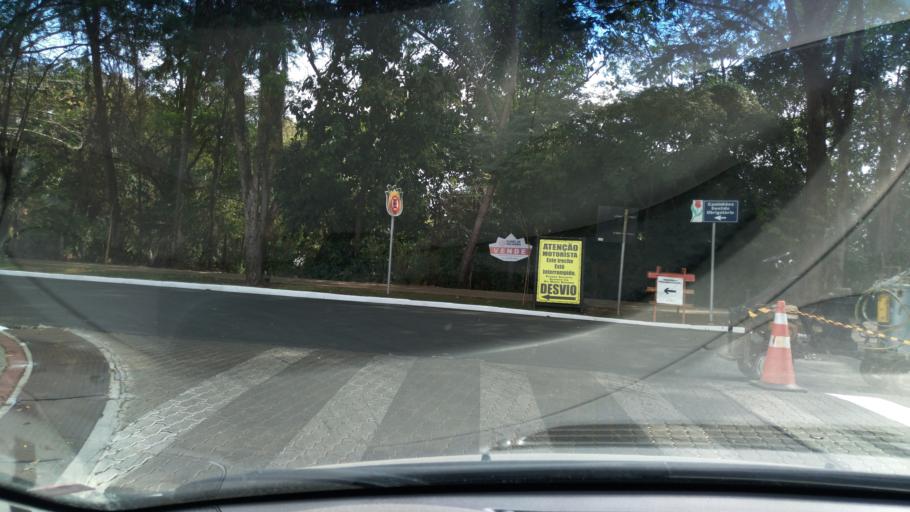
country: BR
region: Sao Paulo
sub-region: Jaguariuna
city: Jaguariuna
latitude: -22.6317
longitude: -47.0577
